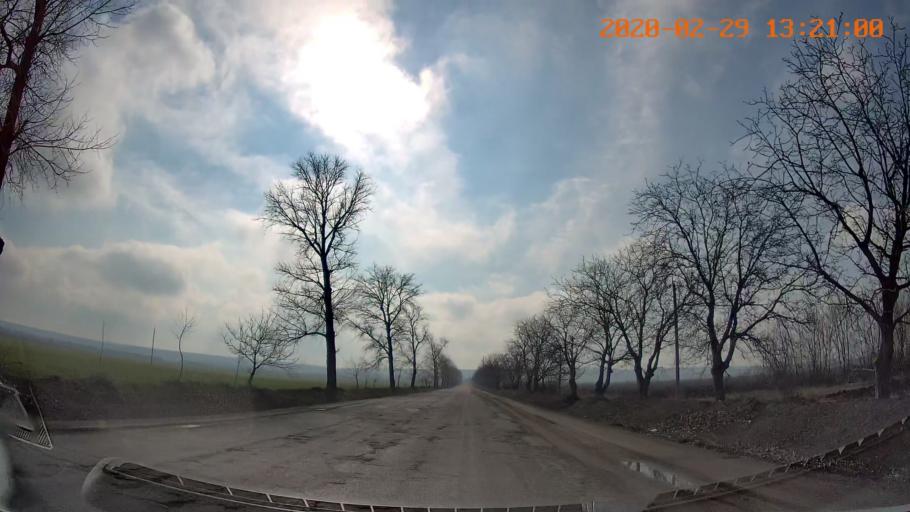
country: MD
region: Telenesti
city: Camenca
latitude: 47.9740
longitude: 28.6366
